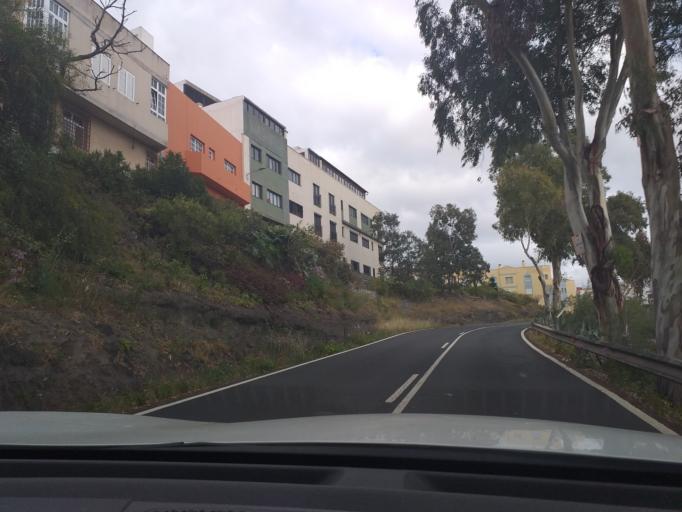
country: ES
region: Canary Islands
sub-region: Provincia de Las Palmas
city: Arucas
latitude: 28.1108
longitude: -15.5074
